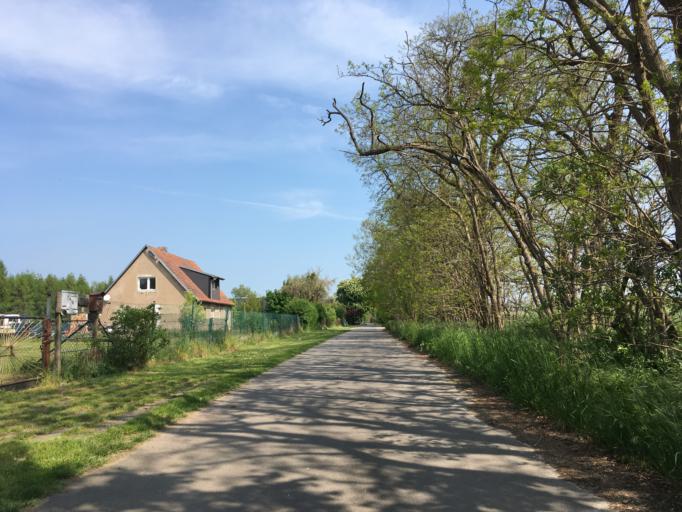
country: DE
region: Brandenburg
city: Altlandsberg
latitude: 52.5967
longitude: 13.7276
